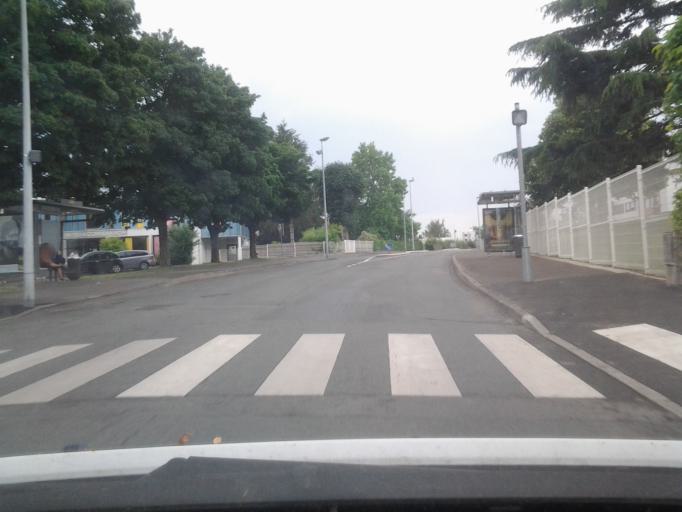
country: FR
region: Pays de la Loire
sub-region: Departement de la Vendee
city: La Roche-sur-Yon
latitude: 46.6761
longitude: -1.4183
